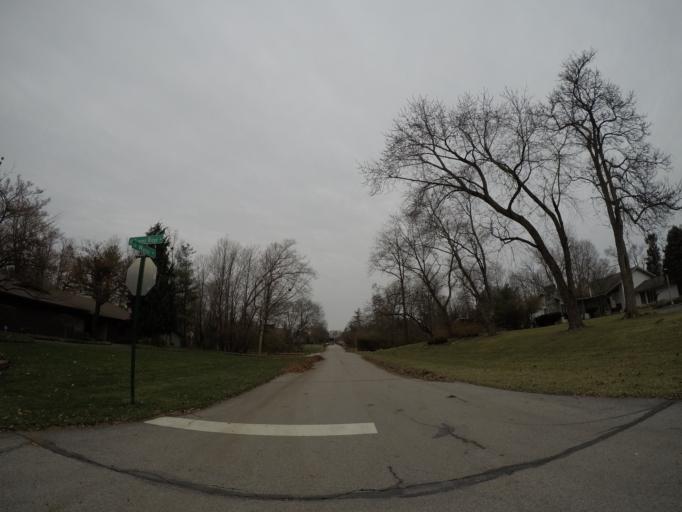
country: US
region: Ohio
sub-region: Franklin County
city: Dublin
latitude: 40.0583
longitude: -83.0894
